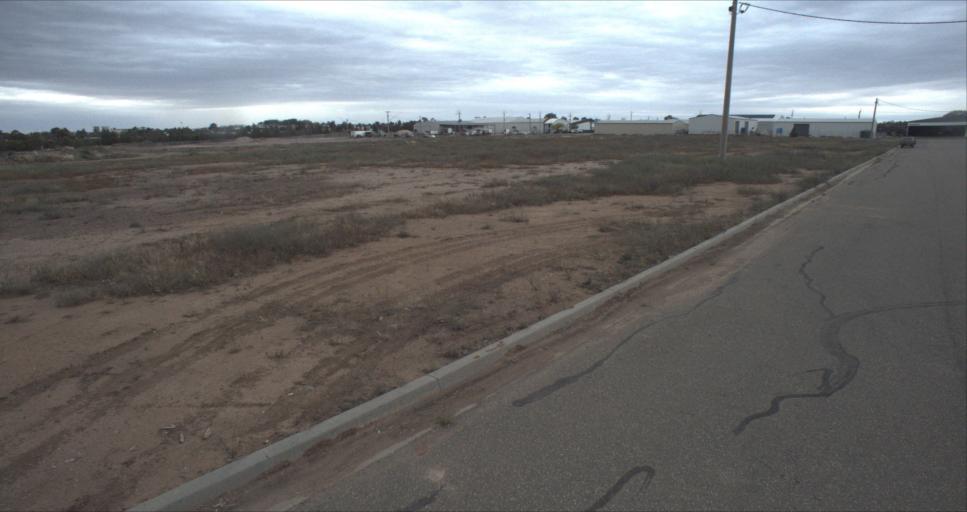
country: AU
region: New South Wales
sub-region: Leeton
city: Leeton
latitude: -34.5438
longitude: 146.3900
